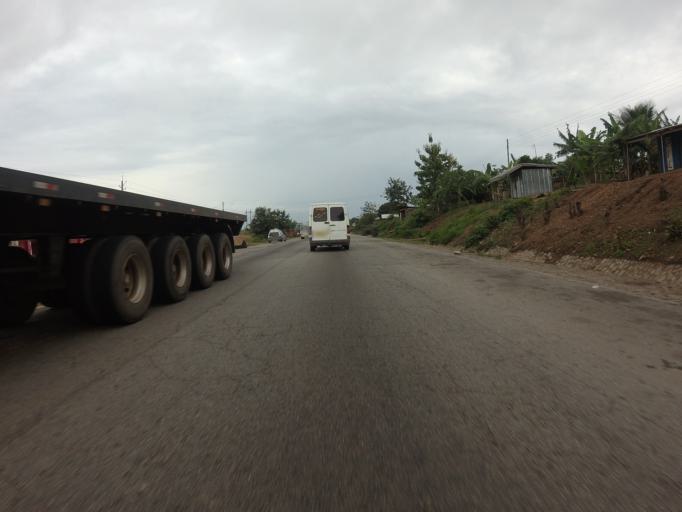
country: GH
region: Ashanti
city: Konongo
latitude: 6.6158
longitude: -1.1584
